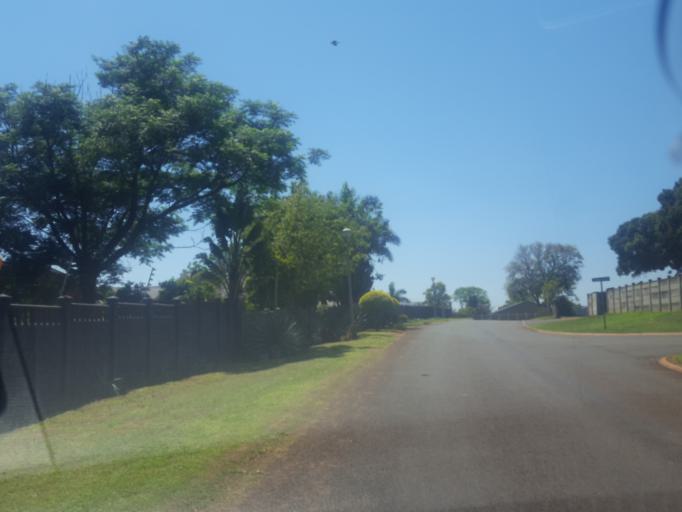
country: ZA
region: KwaZulu-Natal
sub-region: uThungulu District Municipality
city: Empangeni
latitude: -28.7478
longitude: 31.9057
